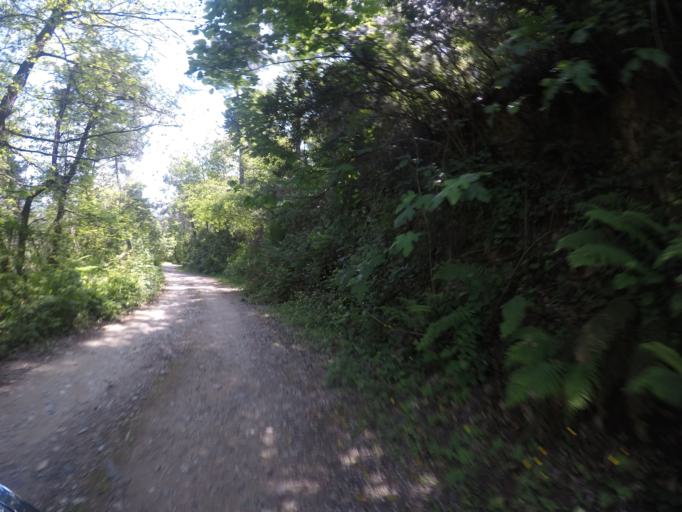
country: IT
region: Tuscany
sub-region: Provincia di Massa-Carrara
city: Carrara
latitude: 44.0628
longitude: 10.1020
